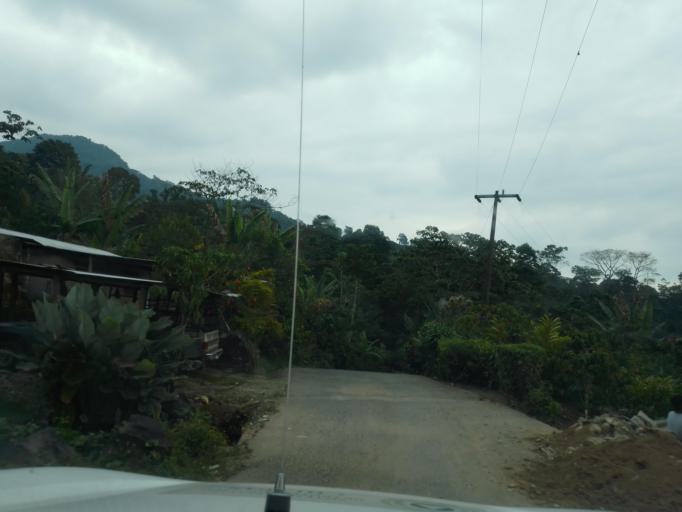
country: MX
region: Chiapas
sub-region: Union Juarez
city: Santo Domingo
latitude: 15.0524
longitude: -92.1220
